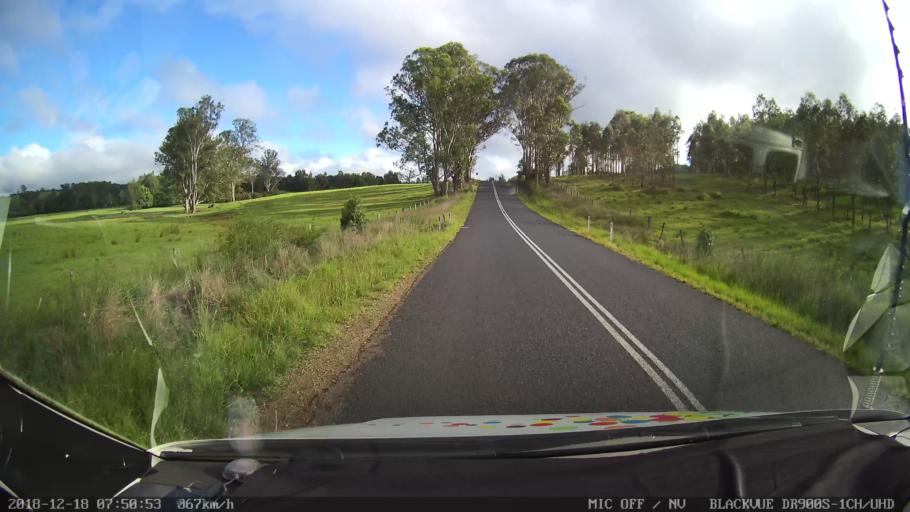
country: AU
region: New South Wales
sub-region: Kyogle
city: Kyogle
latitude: -28.4413
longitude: 152.5743
